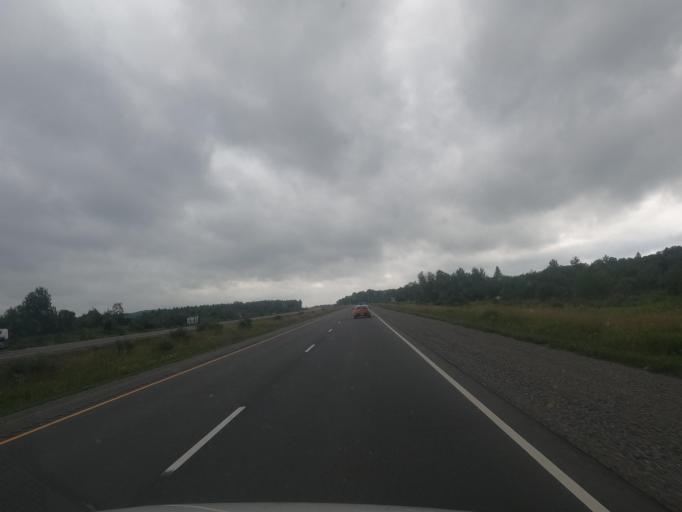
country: CA
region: Ontario
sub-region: Algoma
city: Sault Ste. Marie
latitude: 46.4790
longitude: -84.0522
